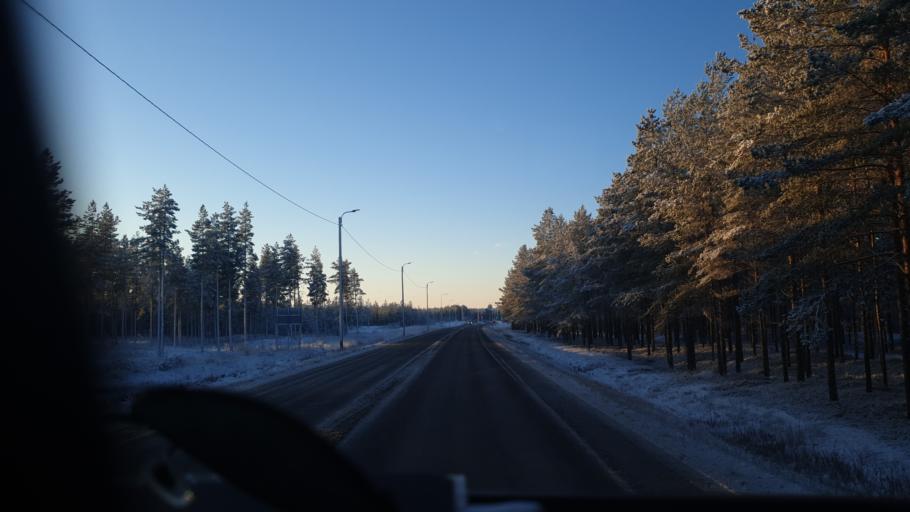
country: FI
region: Northern Ostrobothnia
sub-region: Ylivieska
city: Kalajoki
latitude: 64.2333
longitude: 23.8249
